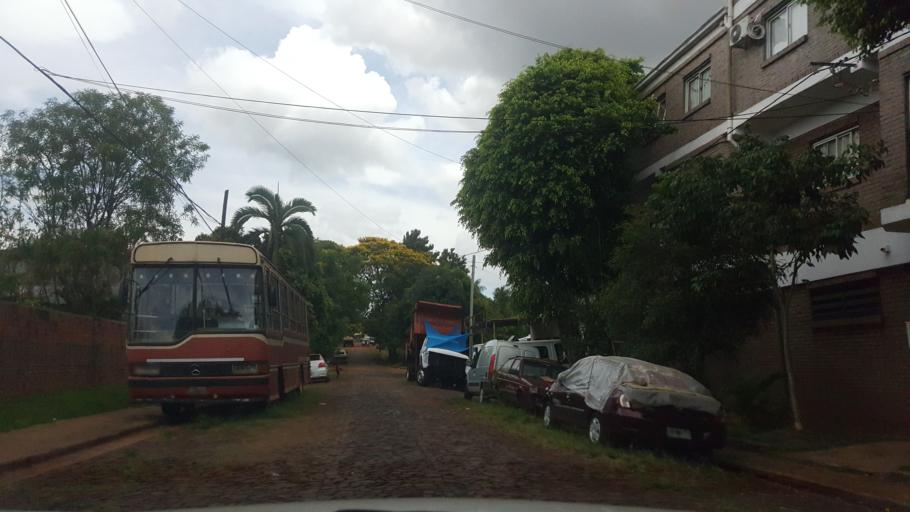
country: AR
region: Misiones
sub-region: Departamento de Capital
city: Posadas
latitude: -27.3955
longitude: -55.8960
